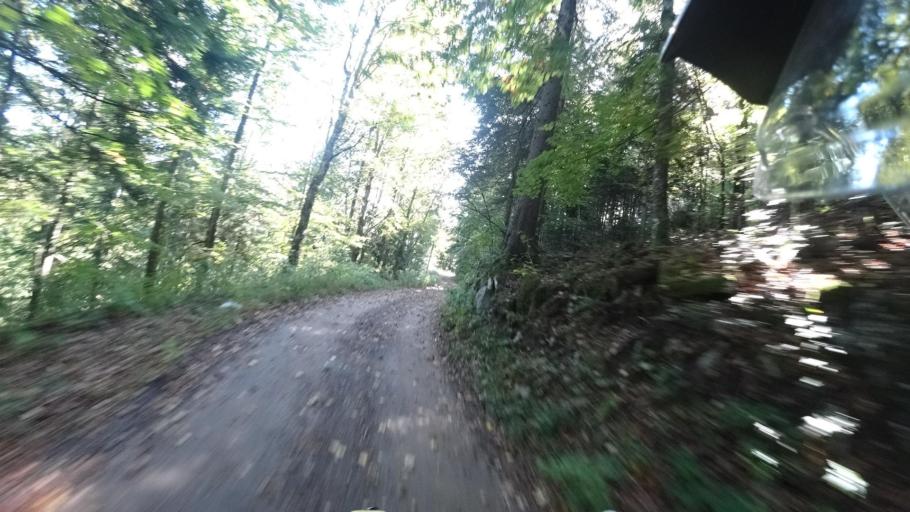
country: HR
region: Primorsko-Goranska
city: Vrbovsko
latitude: 45.2641
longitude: 15.1035
